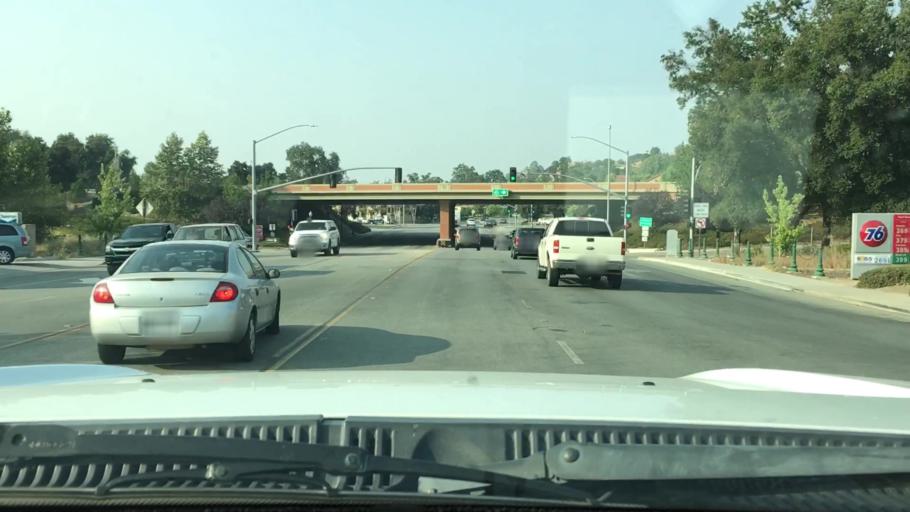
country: US
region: California
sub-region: San Luis Obispo County
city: Atascadero
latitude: 35.4843
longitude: -120.6654
